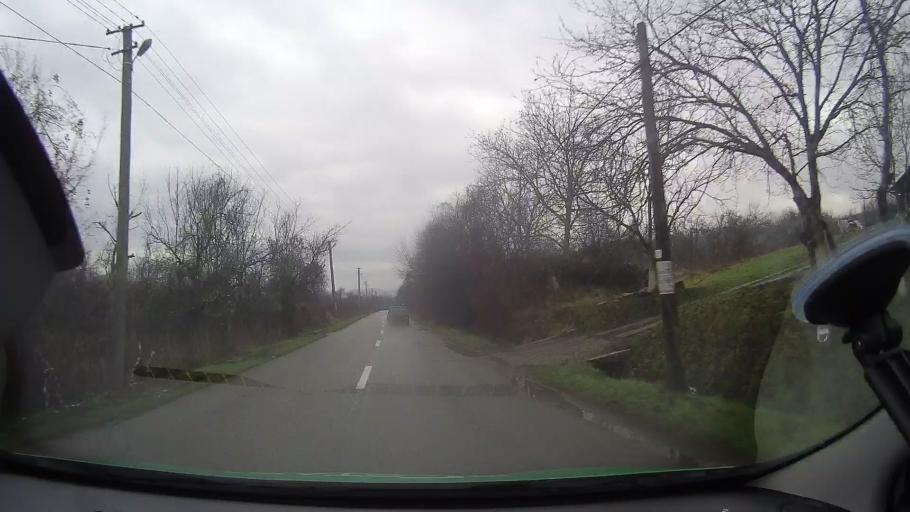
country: RO
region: Arad
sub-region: Comuna Gurahont
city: Gurahont
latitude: 46.2636
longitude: 22.3407
